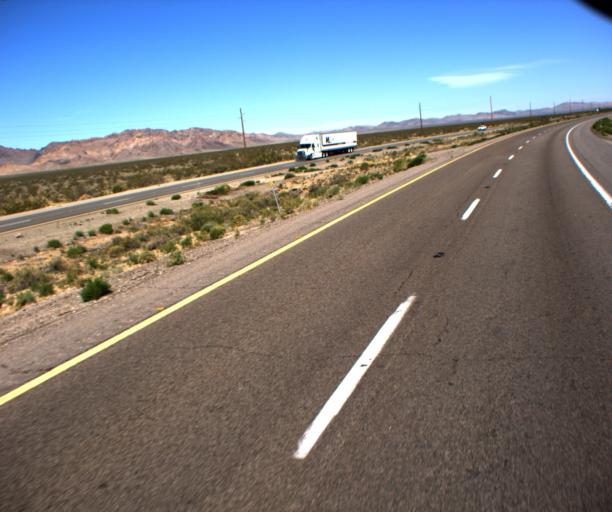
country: US
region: Arizona
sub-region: Mohave County
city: Dolan Springs
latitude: 35.6103
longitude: -114.4110
